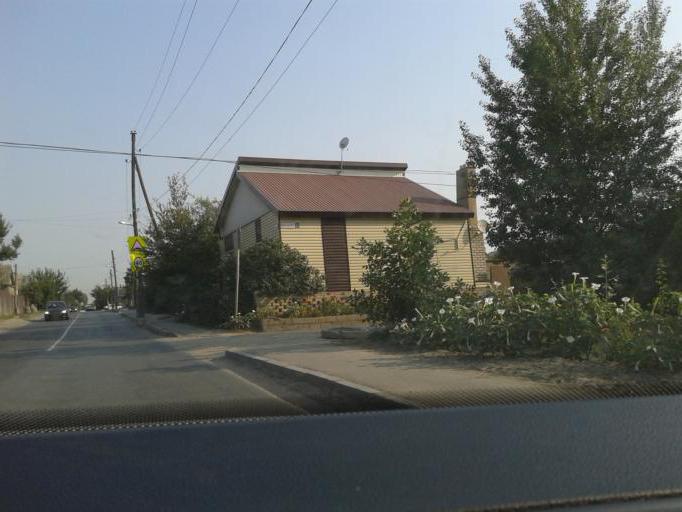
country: RU
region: Volgograd
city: Volgograd
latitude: 48.6998
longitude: 44.4489
